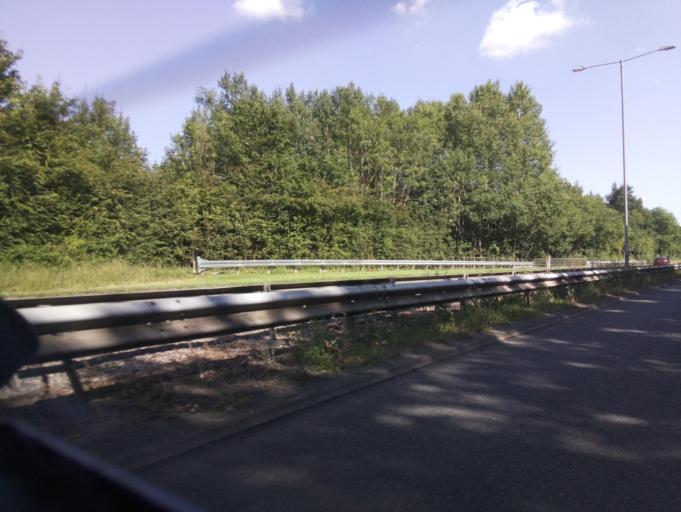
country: GB
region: England
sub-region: Worcestershire
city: Redditch
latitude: 52.3047
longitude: -1.9764
